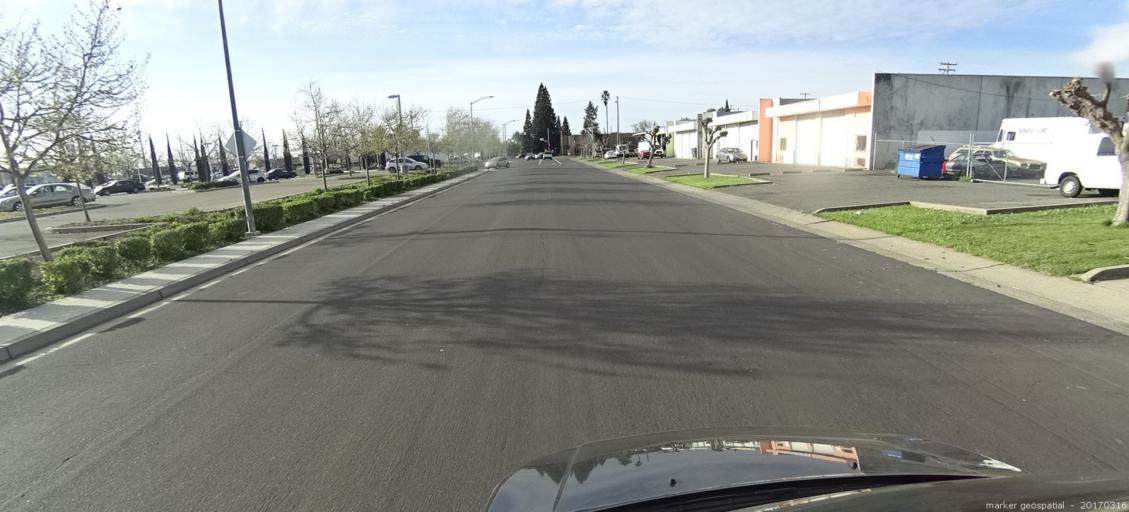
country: US
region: California
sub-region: Sacramento County
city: Parkway
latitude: 38.5118
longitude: -121.4773
